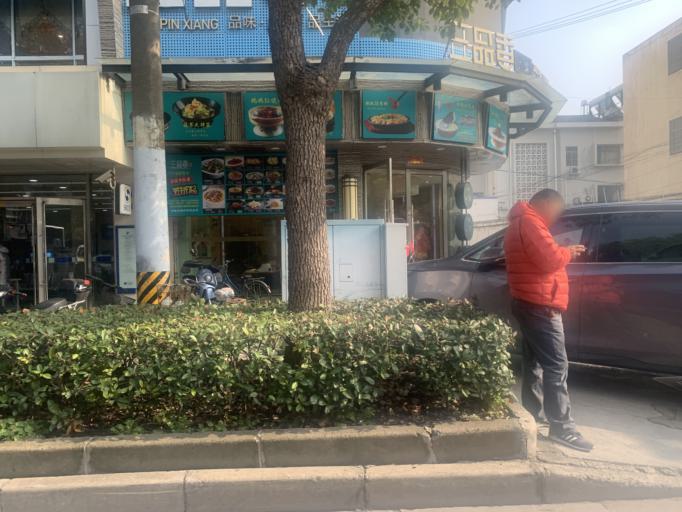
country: CN
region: Shanghai Shi
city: Huamu
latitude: 31.1871
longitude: 121.5140
